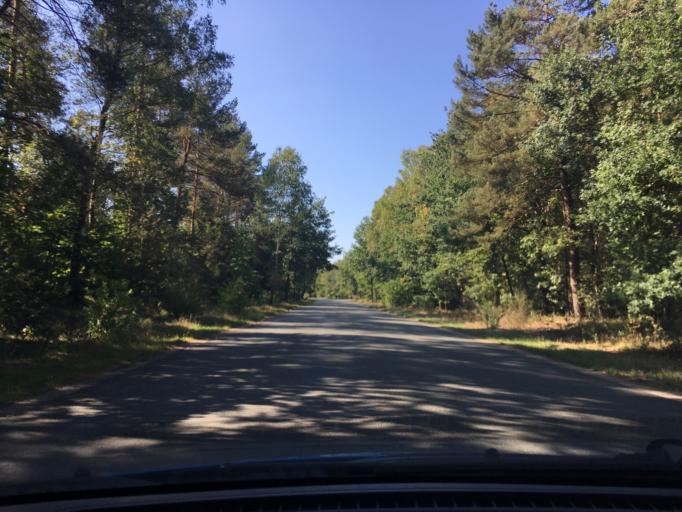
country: DE
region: Lower Saxony
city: Munster
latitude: 52.9651
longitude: 10.1355
